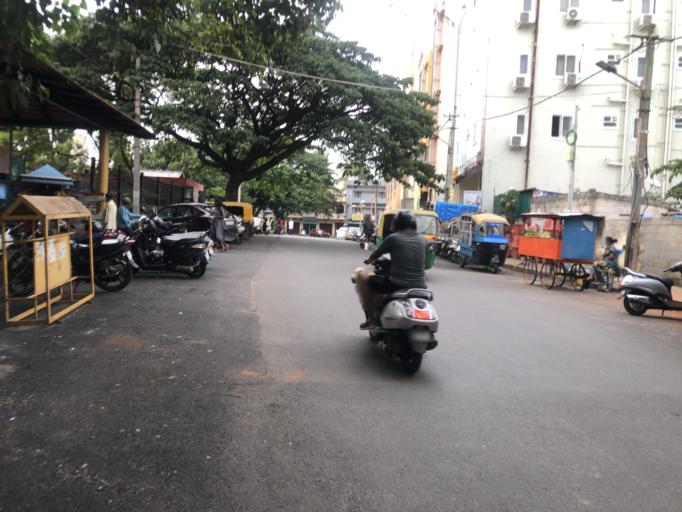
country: IN
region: Karnataka
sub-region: Bangalore Urban
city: Bangalore
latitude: 12.9397
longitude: 77.5477
